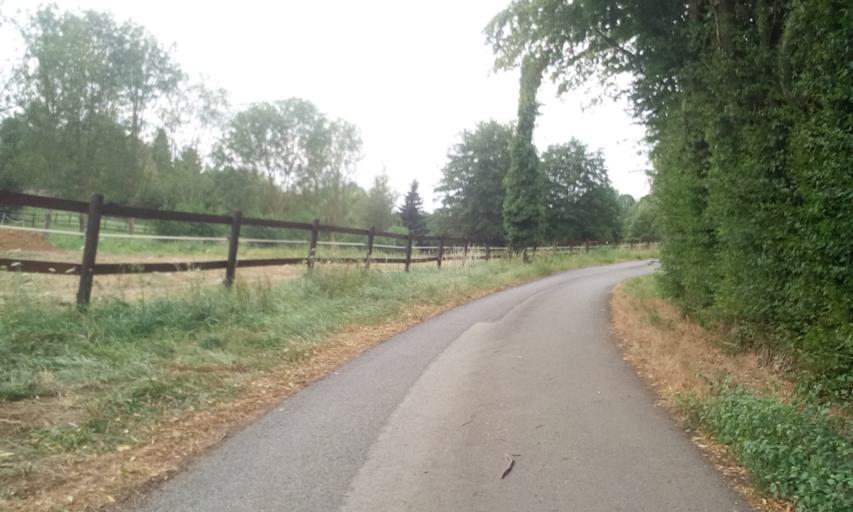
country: FR
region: Lower Normandy
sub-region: Departement du Calvados
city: Thury-Harcourt
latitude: 48.9894
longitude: -0.4118
